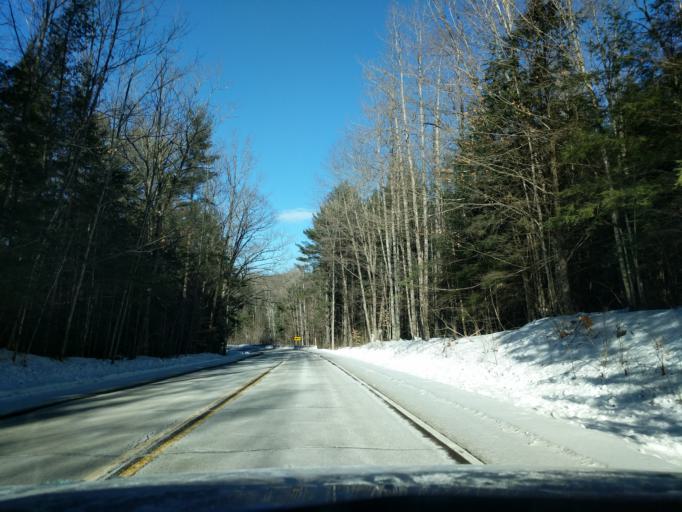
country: US
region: Wisconsin
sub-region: Menominee County
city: Keshena
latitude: 45.1018
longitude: -88.6344
